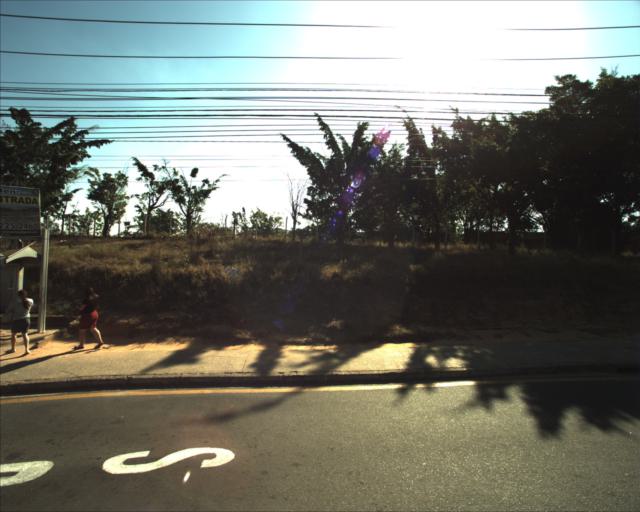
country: BR
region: Sao Paulo
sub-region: Sorocaba
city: Sorocaba
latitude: -23.4599
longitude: -47.4216
